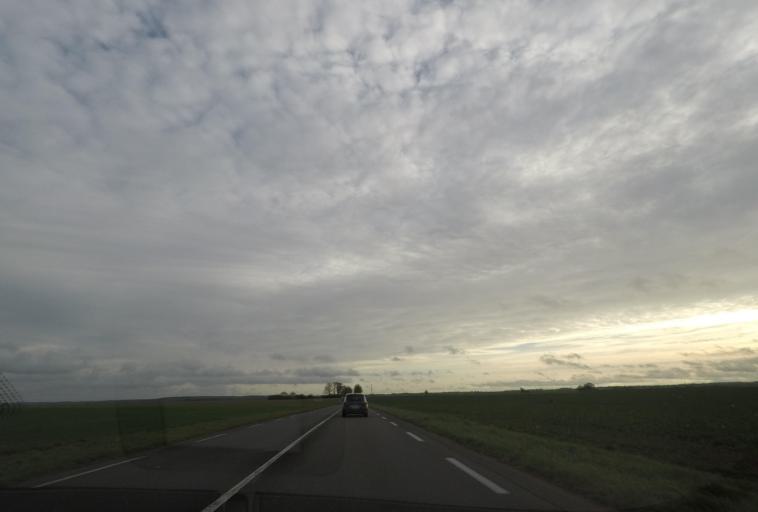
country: FR
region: Centre
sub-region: Departement du Loir-et-Cher
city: Savigny-sur-Braye
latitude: 47.9145
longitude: 0.8059
